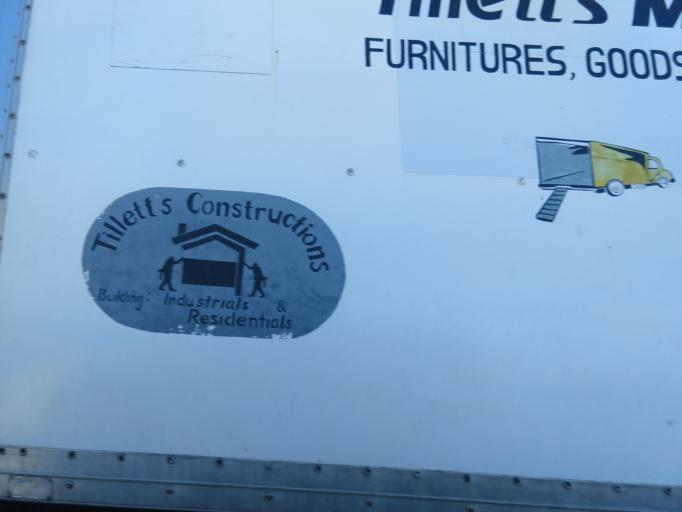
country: BZ
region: Belize
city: Belize City
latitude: 17.5038
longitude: -88.1936
